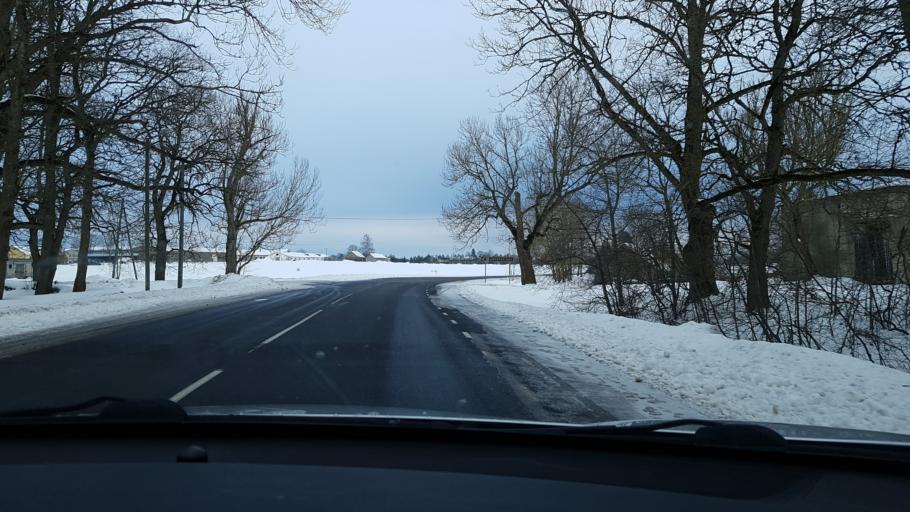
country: EE
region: Jaervamaa
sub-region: Paide linn
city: Paide
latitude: 58.8907
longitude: 25.7138
